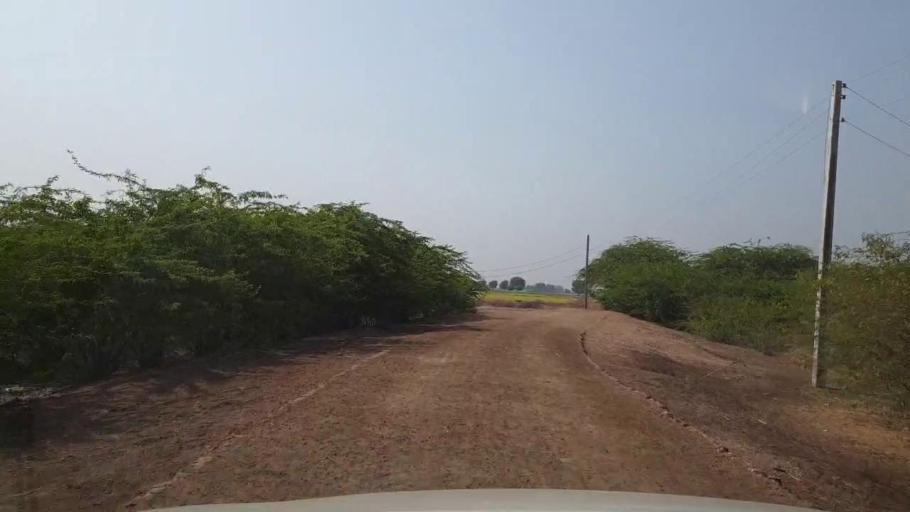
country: PK
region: Sindh
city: Chor
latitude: 25.4749
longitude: 69.7061
